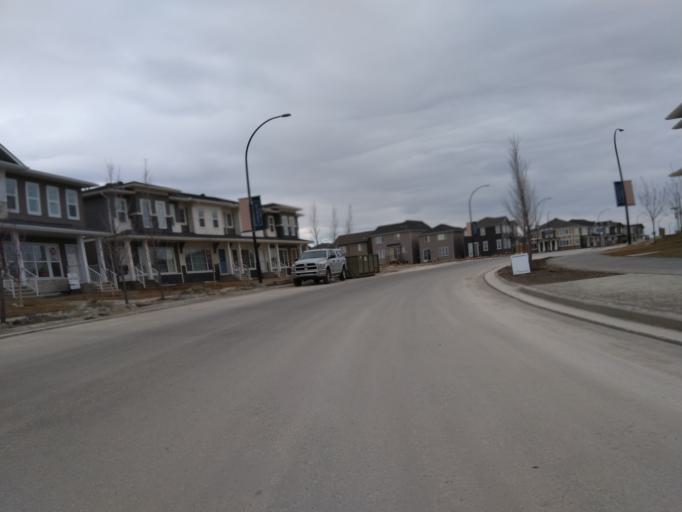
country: CA
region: Alberta
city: Calgary
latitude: 51.1791
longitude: -114.0898
